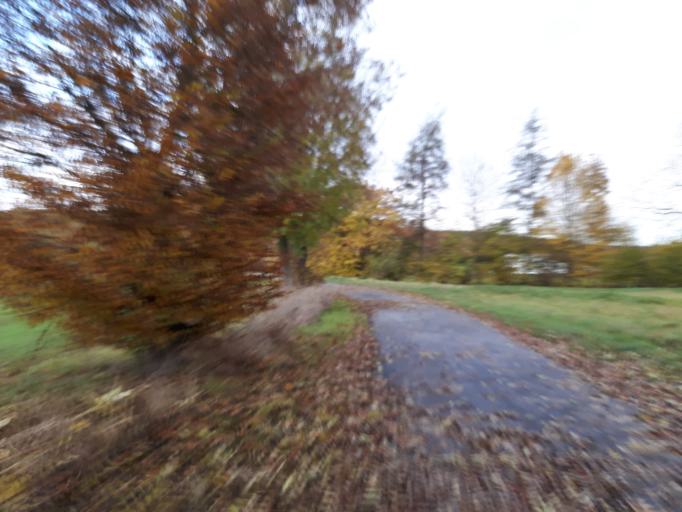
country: DE
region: Baden-Wuerttemberg
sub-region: Regierungsbezirk Stuttgart
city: Eberstadt
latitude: 49.1736
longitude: 9.3102
